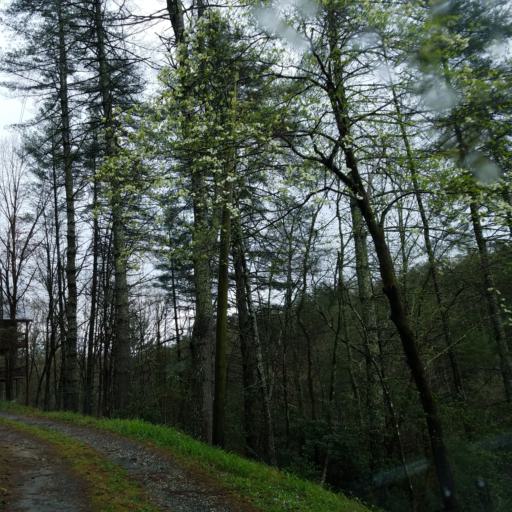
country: US
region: Georgia
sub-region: Fannin County
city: Blue Ridge
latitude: 34.8239
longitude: -84.2371
